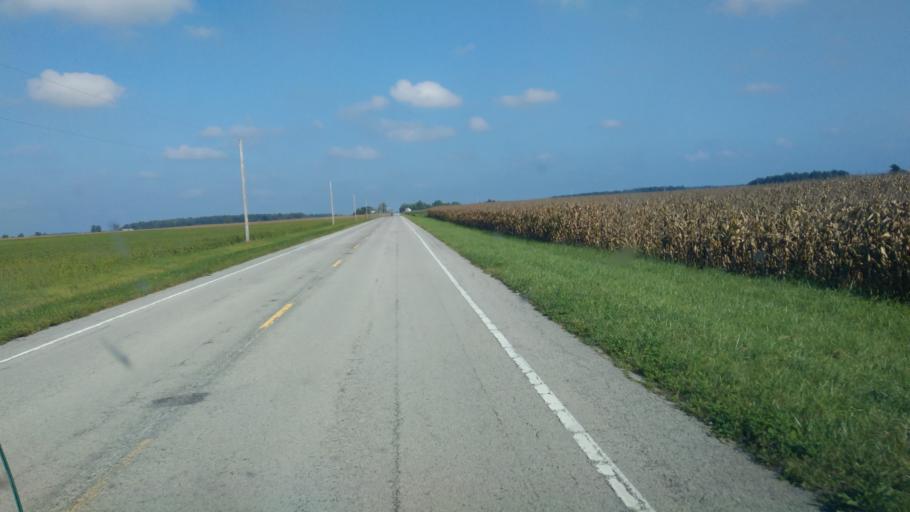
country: US
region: Ohio
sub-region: Hancock County
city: Arlington
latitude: 40.8339
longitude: -83.6212
